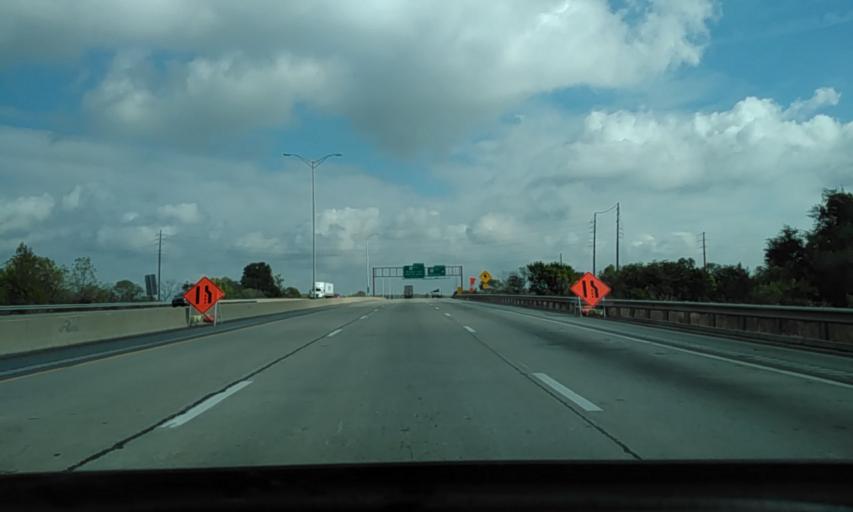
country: US
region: Illinois
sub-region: Saint Clair County
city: Centreville
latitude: 38.5777
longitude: -90.1142
